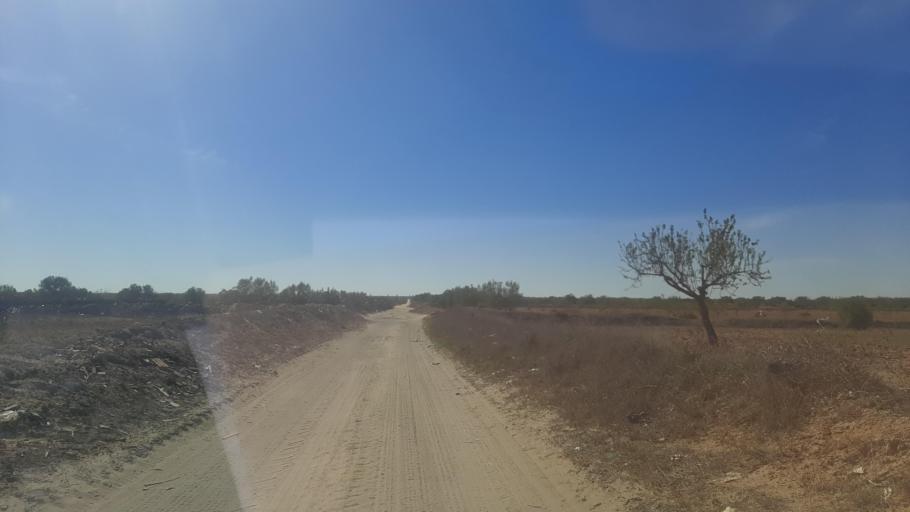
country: TN
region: Safaqis
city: Sfax
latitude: 34.8465
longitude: 10.5613
